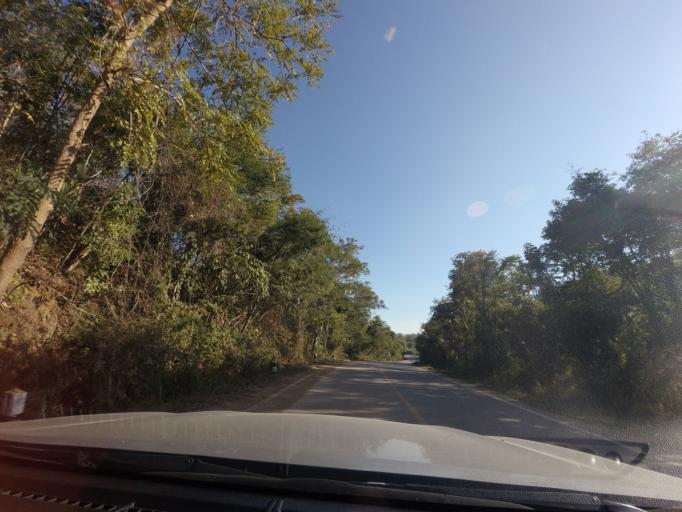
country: TH
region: Lampang
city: Chae Hom
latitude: 18.5393
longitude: 99.6413
